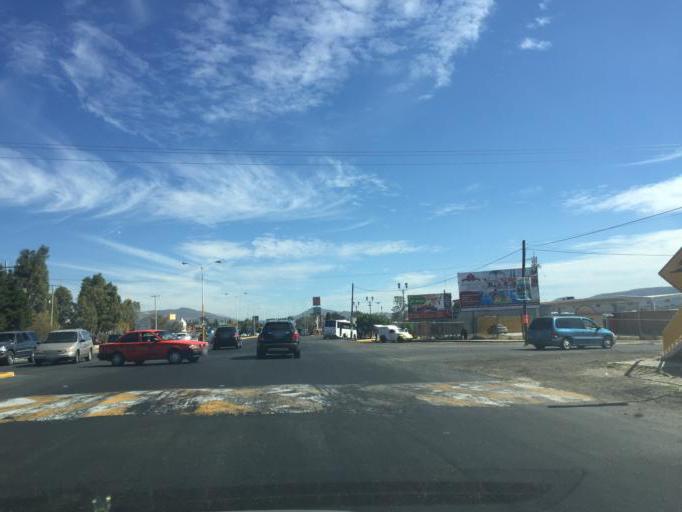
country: MX
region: Queretaro
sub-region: Tequisquiapan
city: Tequisquiapan
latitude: 20.5169
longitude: -99.9000
